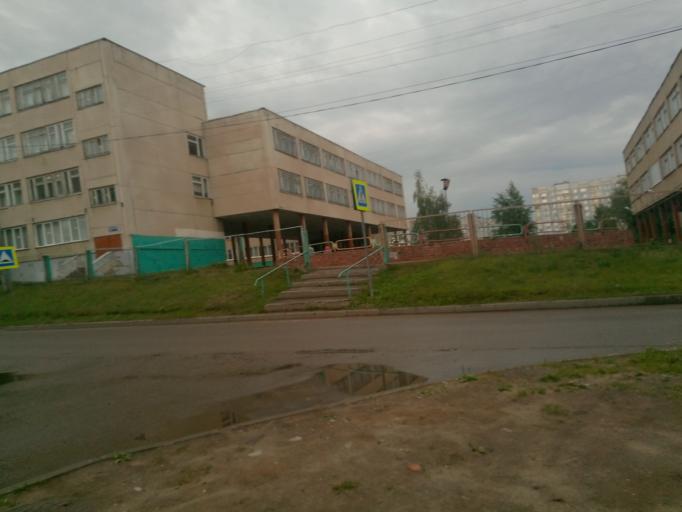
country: RU
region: Jaroslavl
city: Yaroslavl
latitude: 57.6489
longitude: 39.9585
